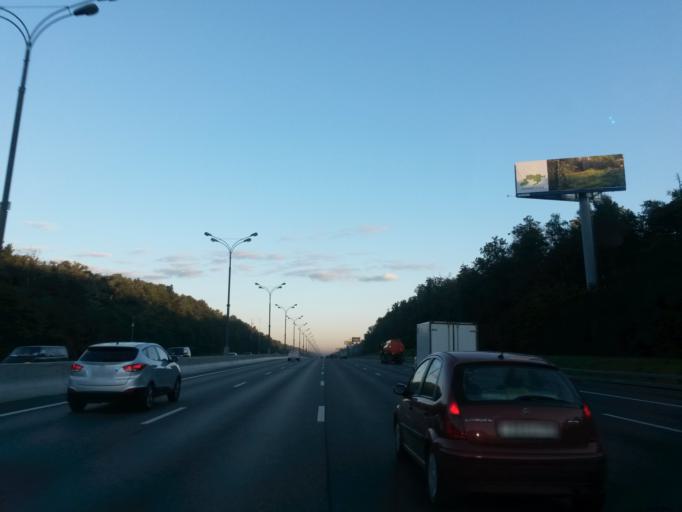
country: RU
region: Moscow
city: Gol'yanovo
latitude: 55.8370
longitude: 37.8145
